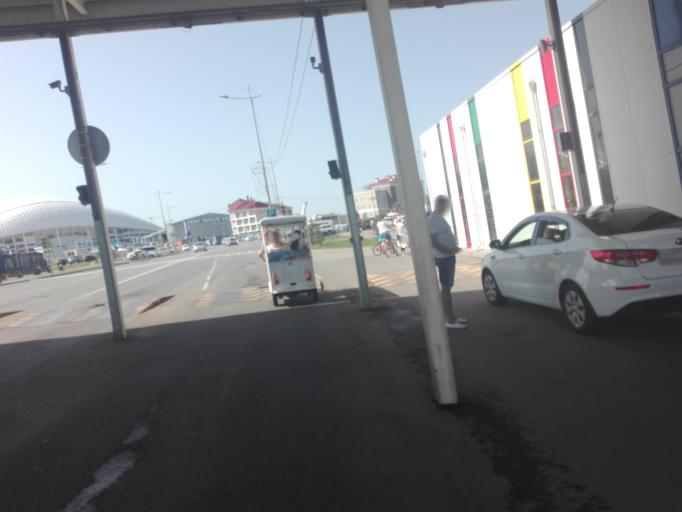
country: RU
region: Krasnodarskiy
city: Adler
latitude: 43.4019
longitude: 39.9647
